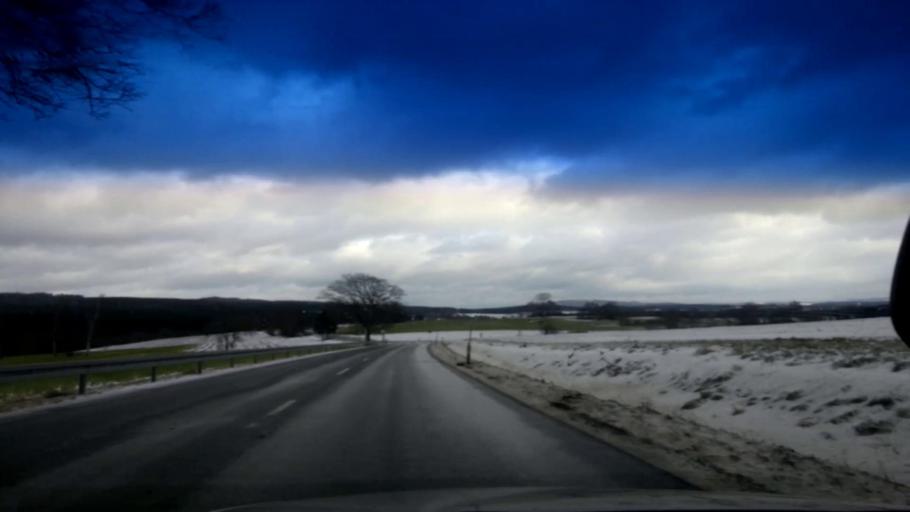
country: DE
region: Bavaria
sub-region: Upper Franconia
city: Weissenstadt
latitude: 50.1112
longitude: 11.8962
